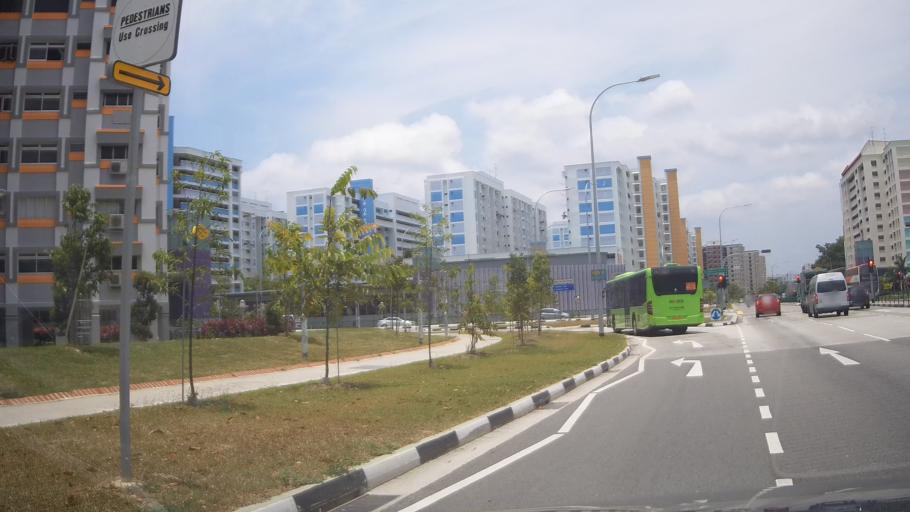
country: SG
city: Singapore
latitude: 1.3576
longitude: 103.9530
